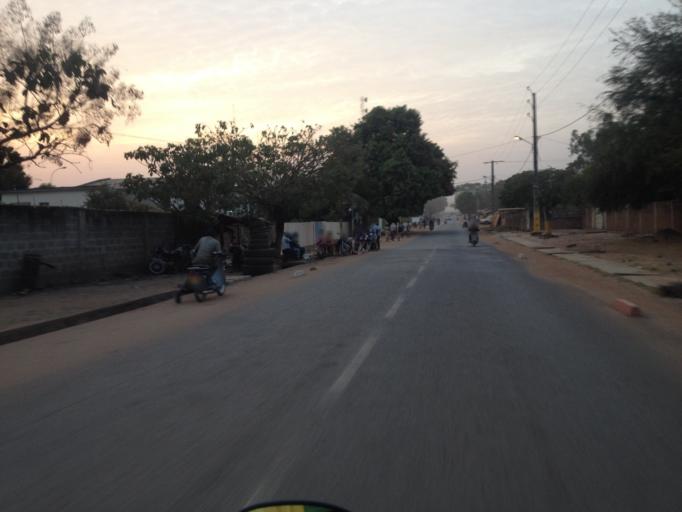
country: BJ
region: Borgou
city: Parakou
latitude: 9.3394
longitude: 2.6334
